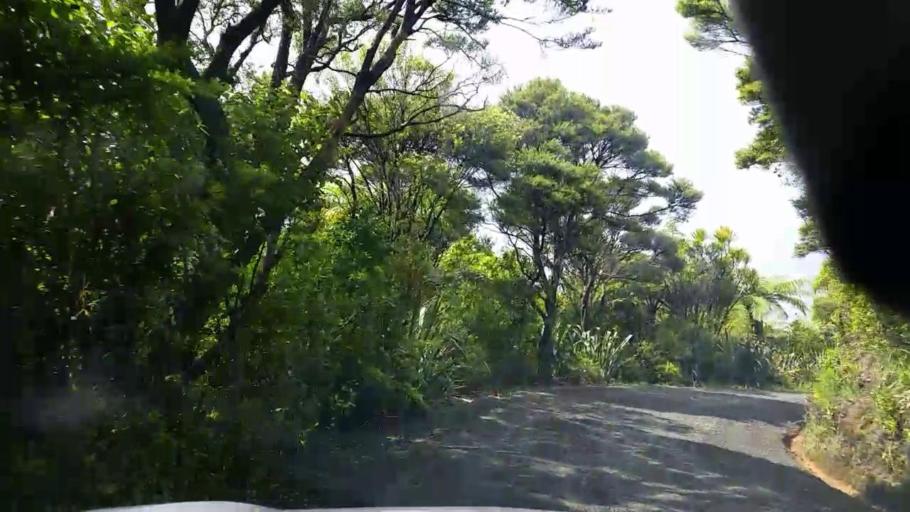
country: NZ
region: Auckland
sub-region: Auckland
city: Muriwai Beach
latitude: -36.9265
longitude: 174.4798
